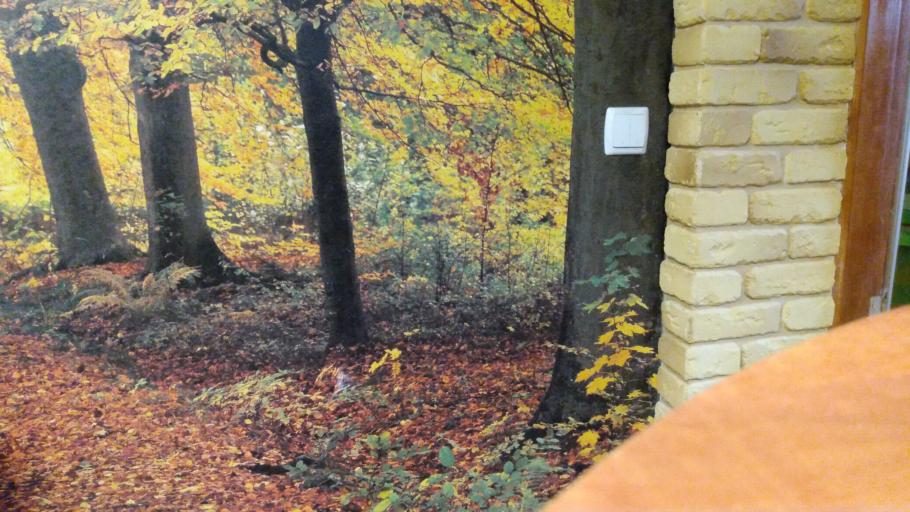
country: RU
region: Pskov
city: Loknya
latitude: 56.9207
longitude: 30.5259
